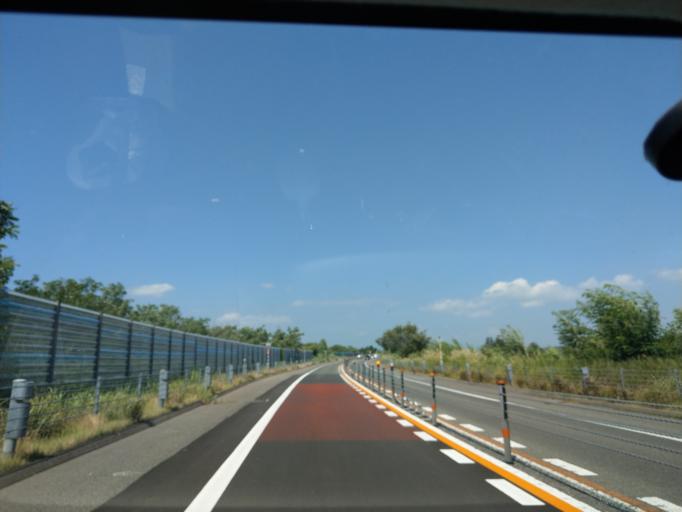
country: JP
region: Akita
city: Yokotemachi
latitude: 39.3385
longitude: 140.5014
